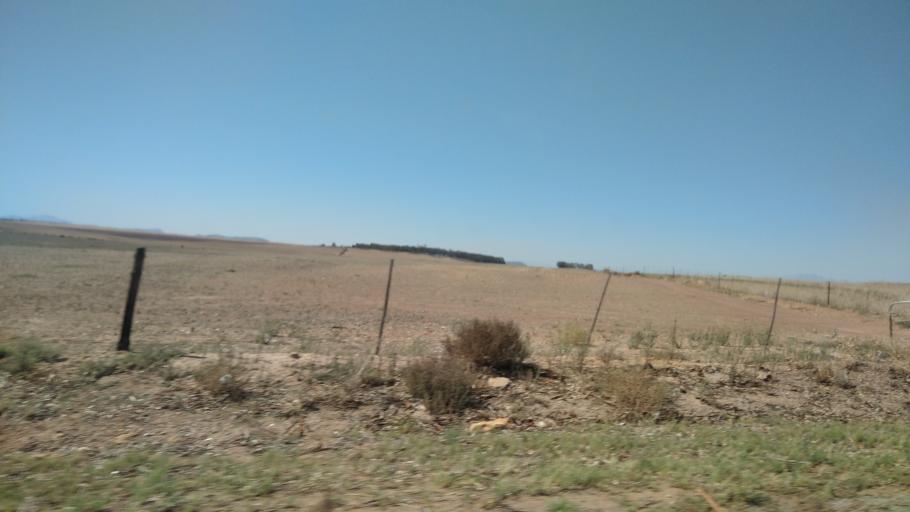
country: ZA
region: Western Cape
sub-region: West Coast District Municipality
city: Moorreesburg
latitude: -33.2160
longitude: 18.5376
